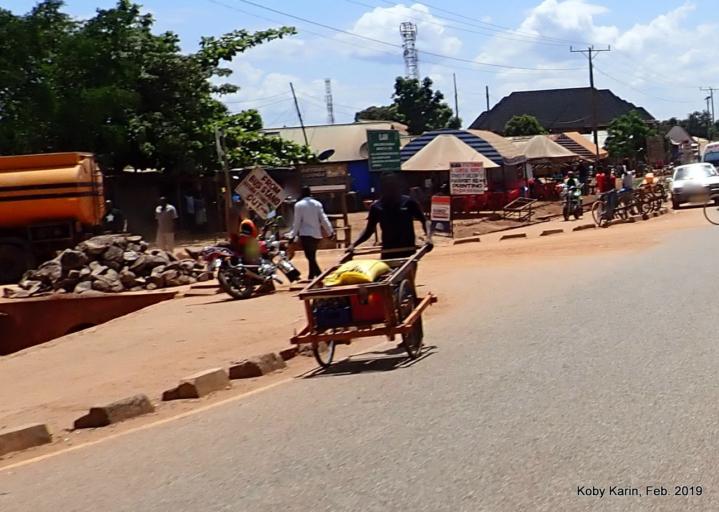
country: TZ
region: Geita
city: Ushirombo
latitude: -3.4688
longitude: 31.8951
